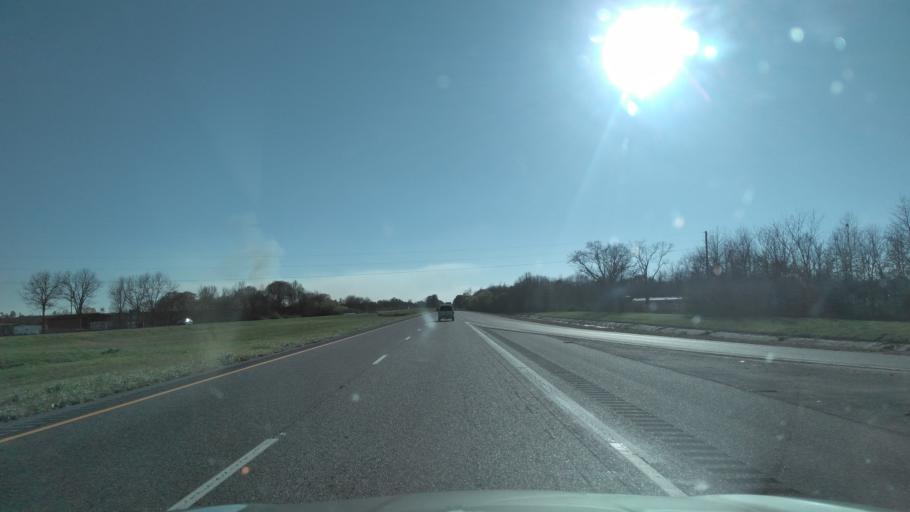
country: US
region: Alabama
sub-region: Escambia County
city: Atmore
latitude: 31.0816
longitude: -87.5382
